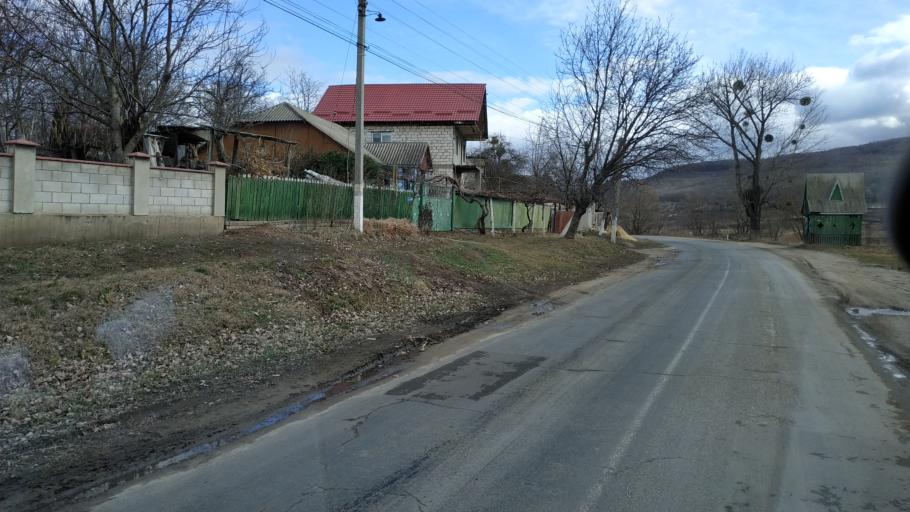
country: MD
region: Calarasi
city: Calarasi
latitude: 47.1325
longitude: 28.3135
